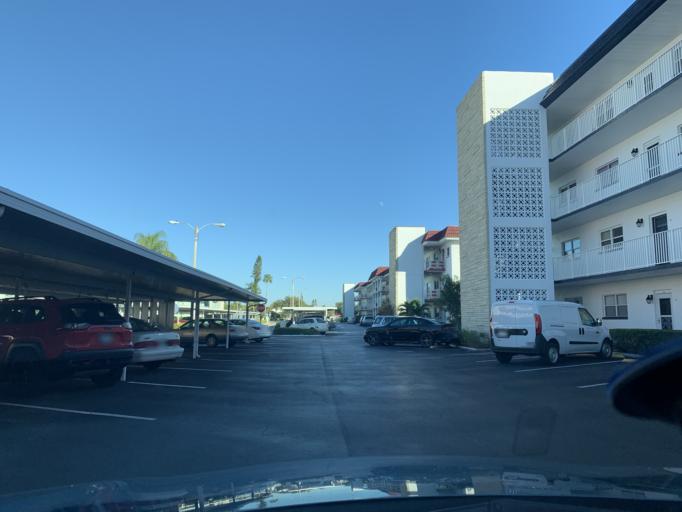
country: US
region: Florida
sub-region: Pinellas County
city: Gulfport
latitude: 27.7401
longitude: -82.7151
